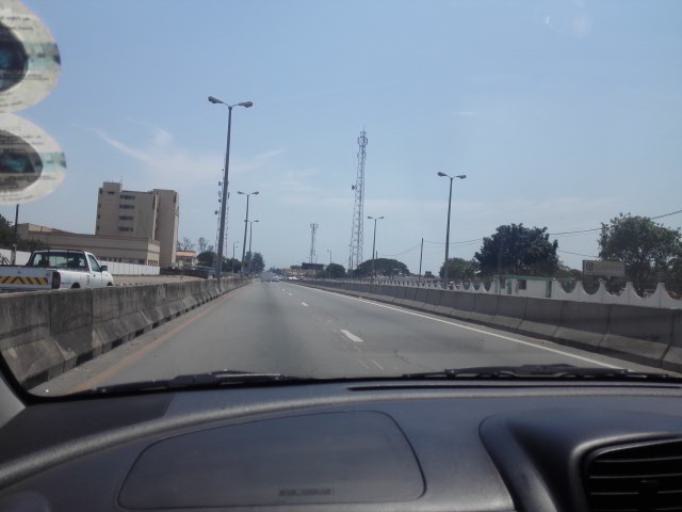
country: MZ
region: Maputo City
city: Maputo
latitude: -25.9376
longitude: 32.5472
